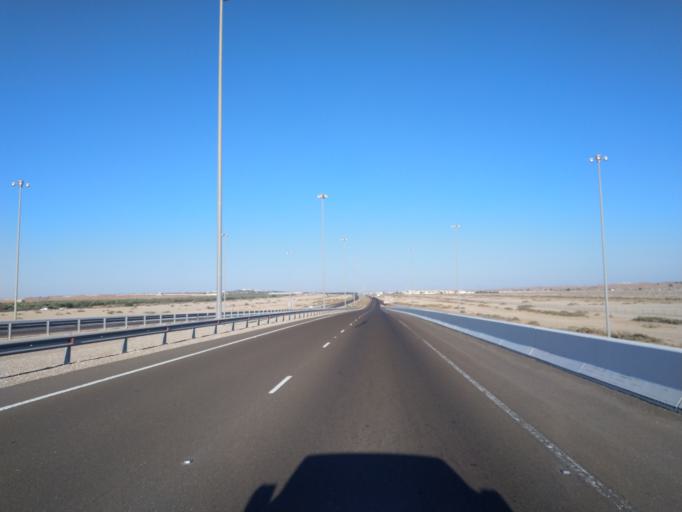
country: OM
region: Al Buraimi
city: Al Buraymi
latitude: 24.5023
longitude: 55.4496
